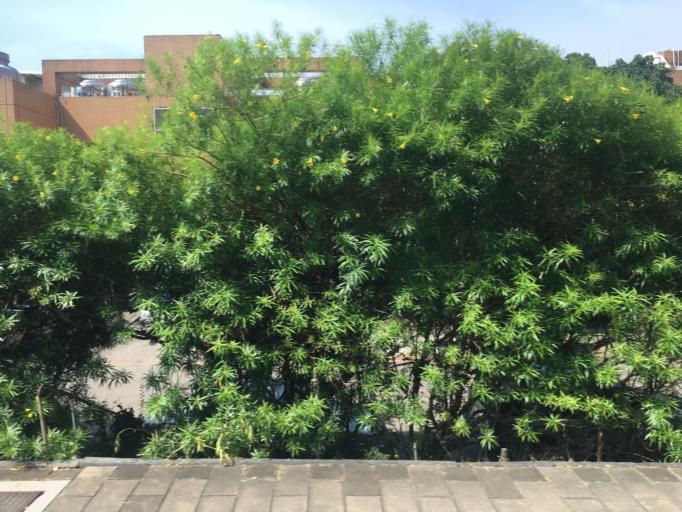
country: TW
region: Taiwan
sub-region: Hsinchu
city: Hsinchu
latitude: 24.7746
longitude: 121.0064
